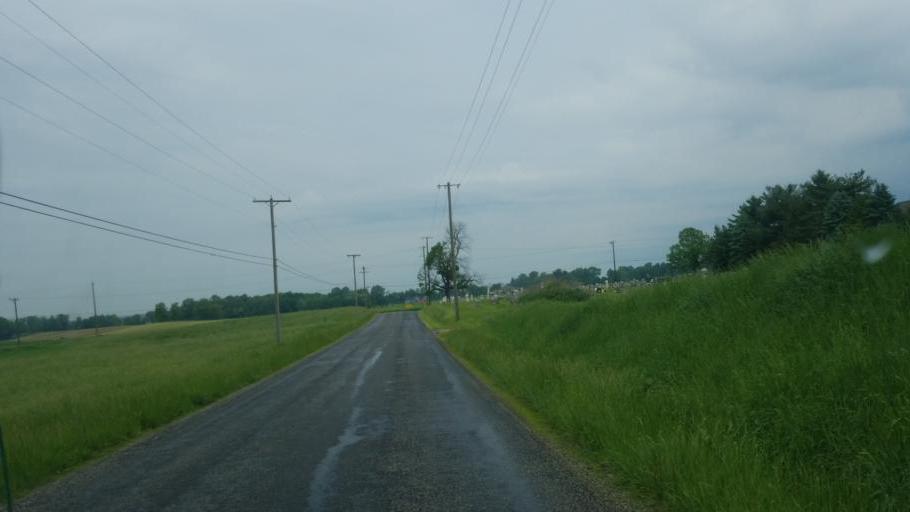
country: US
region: Ohio
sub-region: Wayne County
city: Orrville
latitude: 40.8204
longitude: -81.7328
